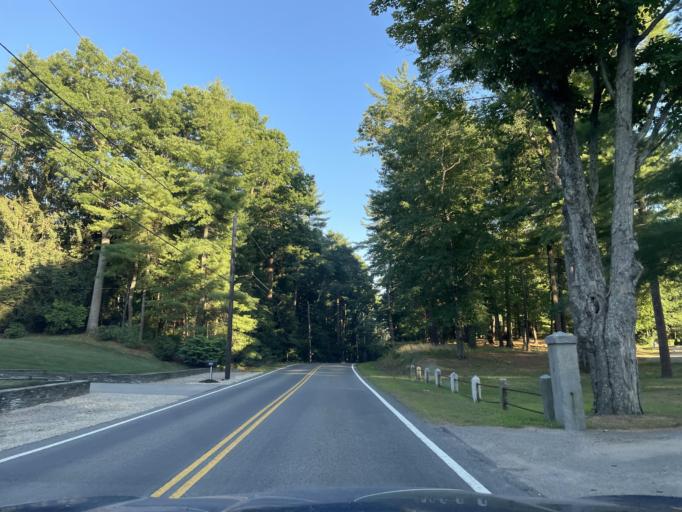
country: US
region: Massachusetts
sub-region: Plymouth County
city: East Bridgewater
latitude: 42.0097
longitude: -70.9580
